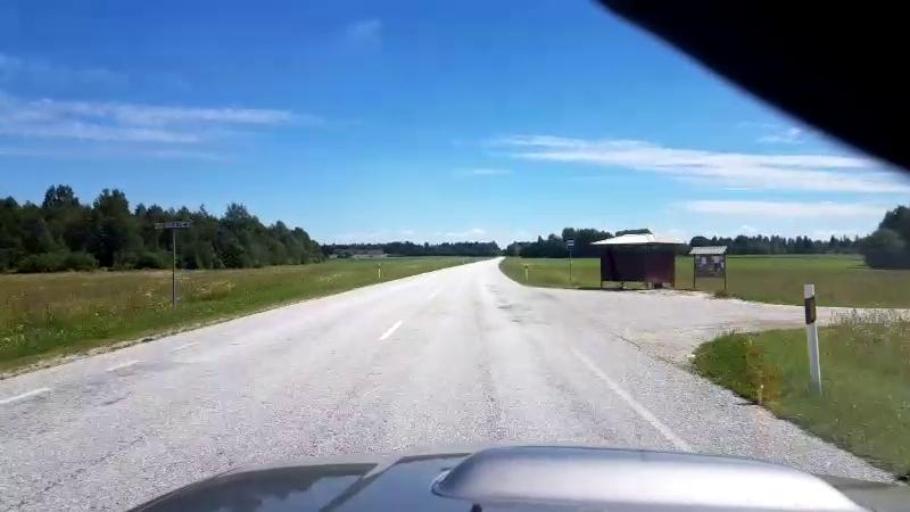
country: EE
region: Laeaene-Virumaa
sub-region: Rakke vald
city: Rakke
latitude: 58.9581
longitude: 26.1679
